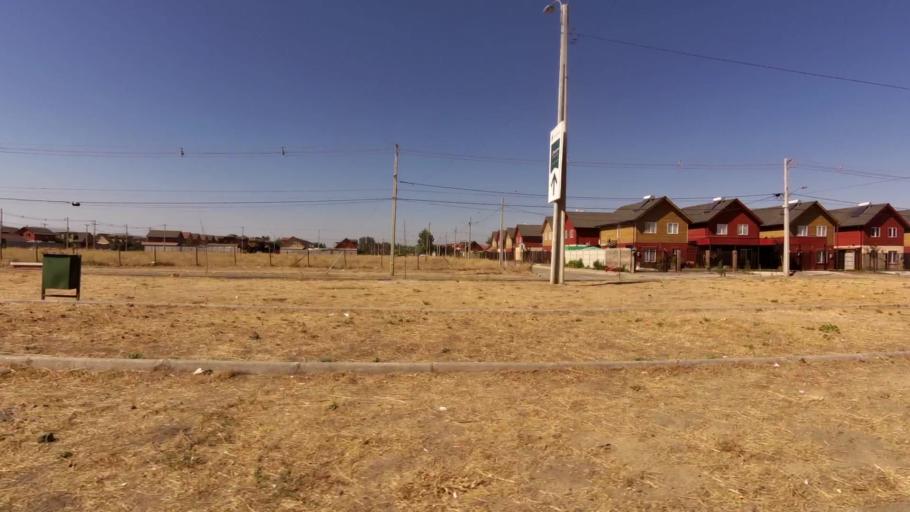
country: CL
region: Maule
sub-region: Provincia de Talca
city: Talca
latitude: -35.4133
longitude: -71.6206
